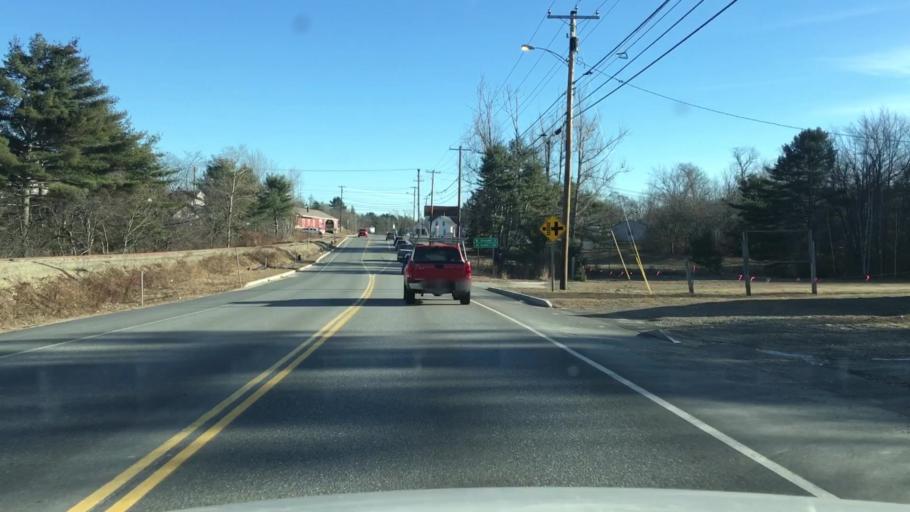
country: US
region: Maine
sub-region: Hancock County
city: Ellsworth
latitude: 44.5636
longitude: -68.4423
